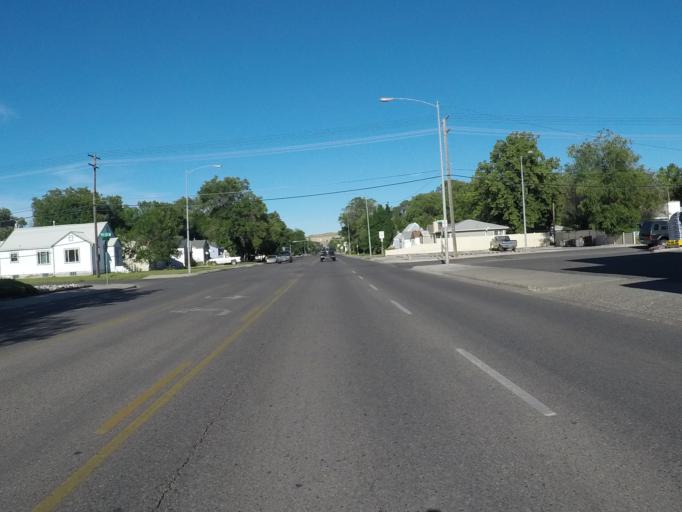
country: US
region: Montana
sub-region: Yellowstone County
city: Billings
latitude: 45.7771
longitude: -108.5390
